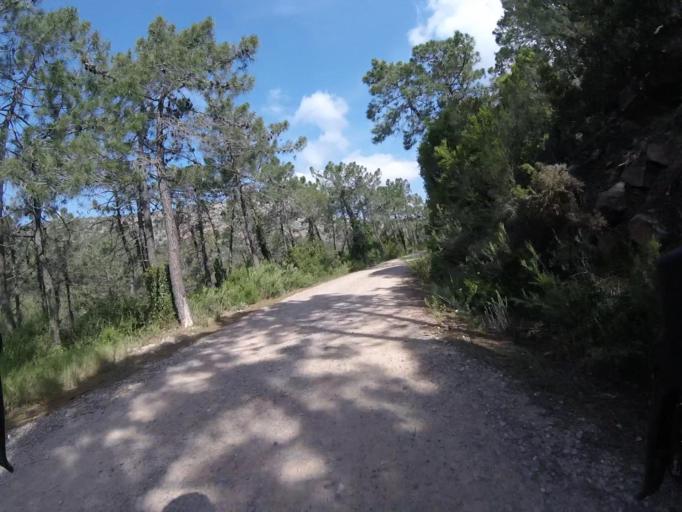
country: ES
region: Valencia
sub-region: Provincia de Castello
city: Cabanes
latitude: 40.0992
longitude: 0.0339
